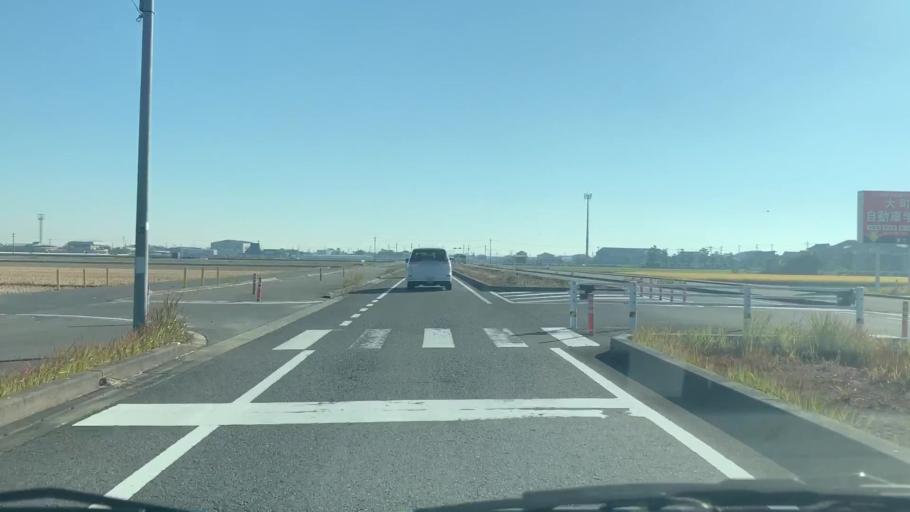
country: JP
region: Saga Prefecture
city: Saga-shi
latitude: 33.2214
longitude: 130.2006
